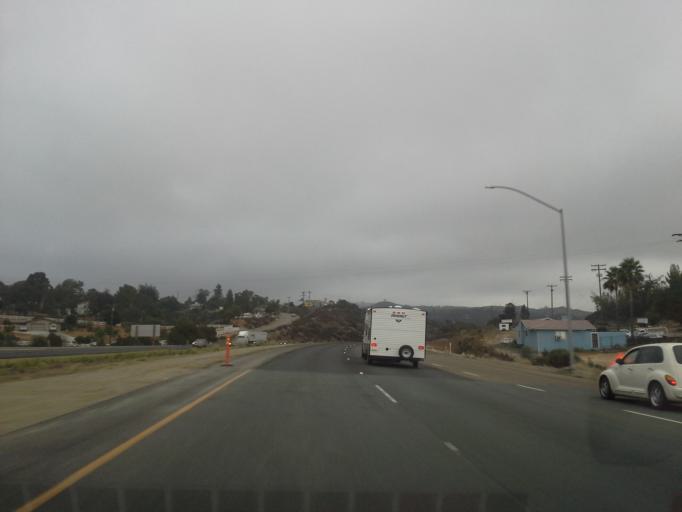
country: US
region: California
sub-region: San Diego County
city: Harbison Canyon
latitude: 32.8568
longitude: -116.8164
